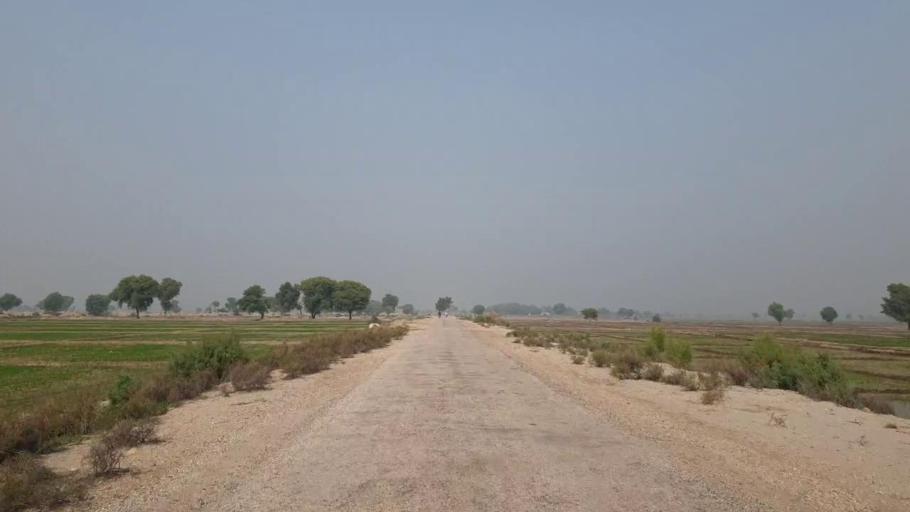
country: PK
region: Sindh
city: Bhan
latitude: 26.5162
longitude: 67.6897
